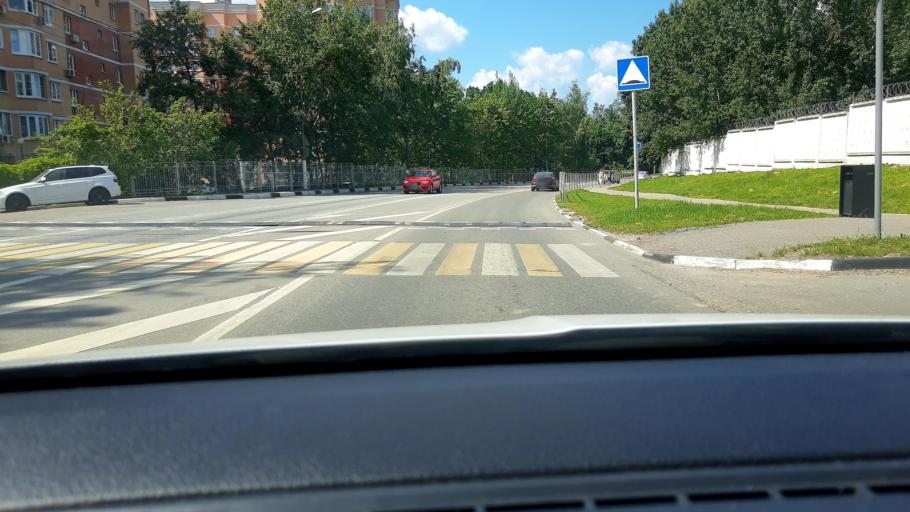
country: RU
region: Moskovskaya
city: Odintsovo
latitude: 55.6884
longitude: 37.2565
